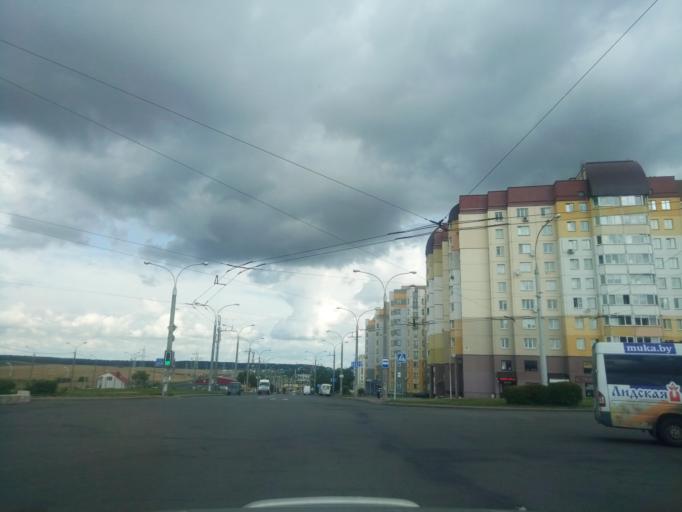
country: BY
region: Minsk
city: Novoye Medvezhino
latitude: 53.8859
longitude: 27.4169
